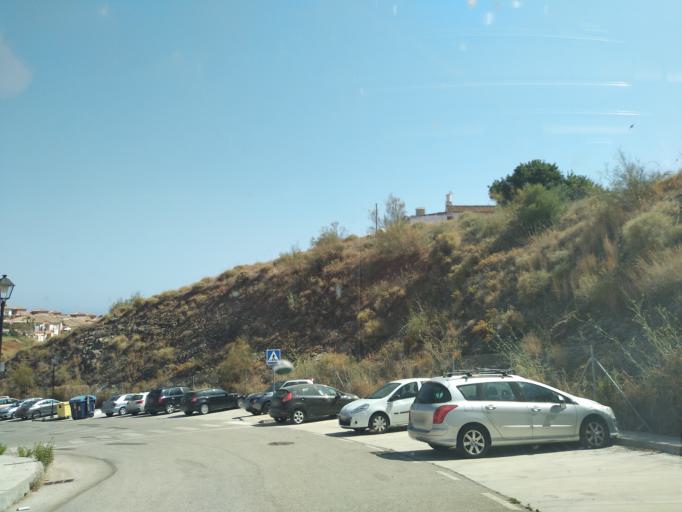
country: ES
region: Andalusia
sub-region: Provincia de Malaga
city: Valdes
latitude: 36.7202
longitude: -4.1999
